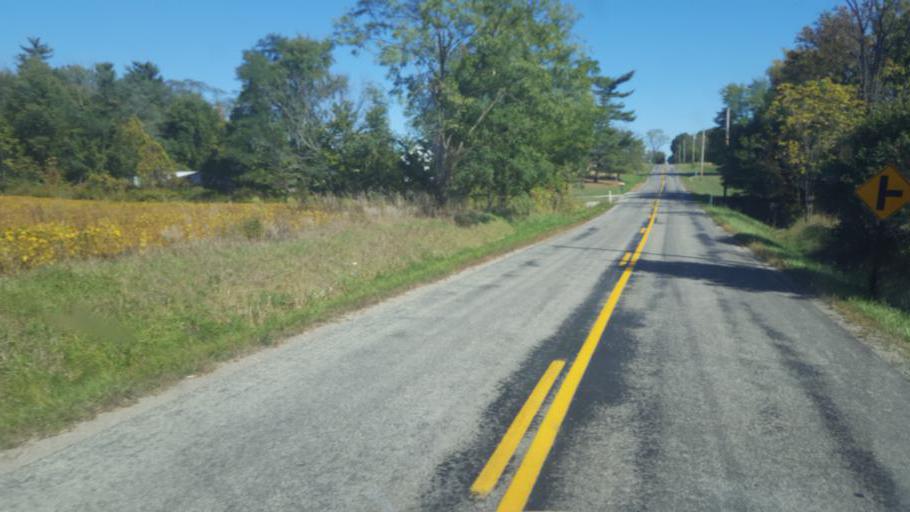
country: US
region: Ohio
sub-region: Huron County
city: New London
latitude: 40.9929
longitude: -82.3526
